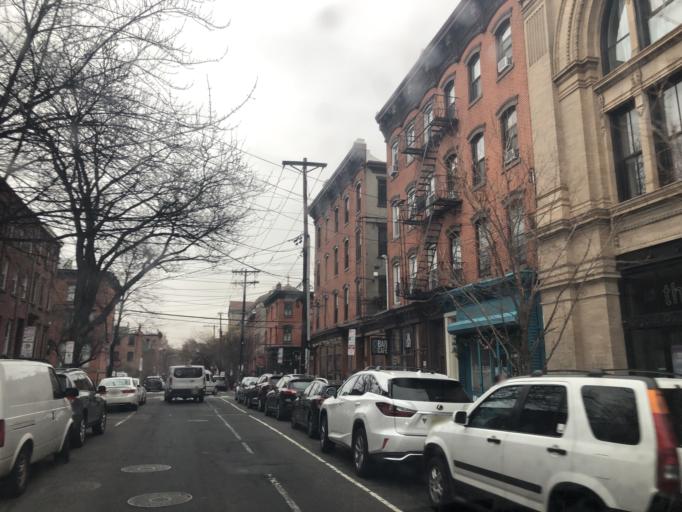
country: US
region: New Jersey
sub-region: Hudson County
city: Hoboken
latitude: 40.7211
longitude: -74.0444
